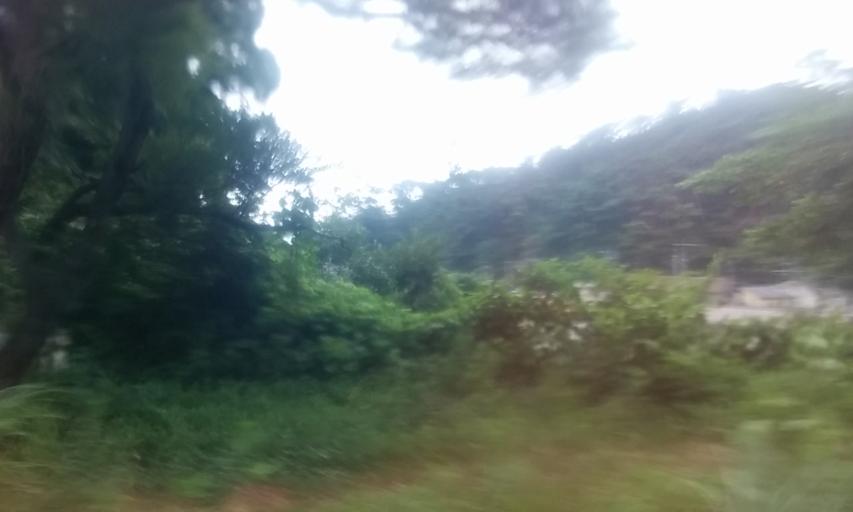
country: JP
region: Miyagi
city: Matsushima
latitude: 38.3625
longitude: 141.0581
